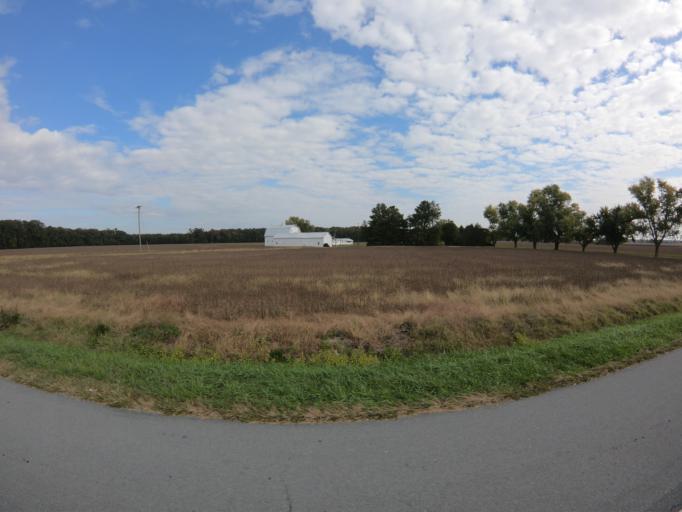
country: US
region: Delaware
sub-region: Sussex County
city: Bridgeville
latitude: 38.7593
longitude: -75.6367
